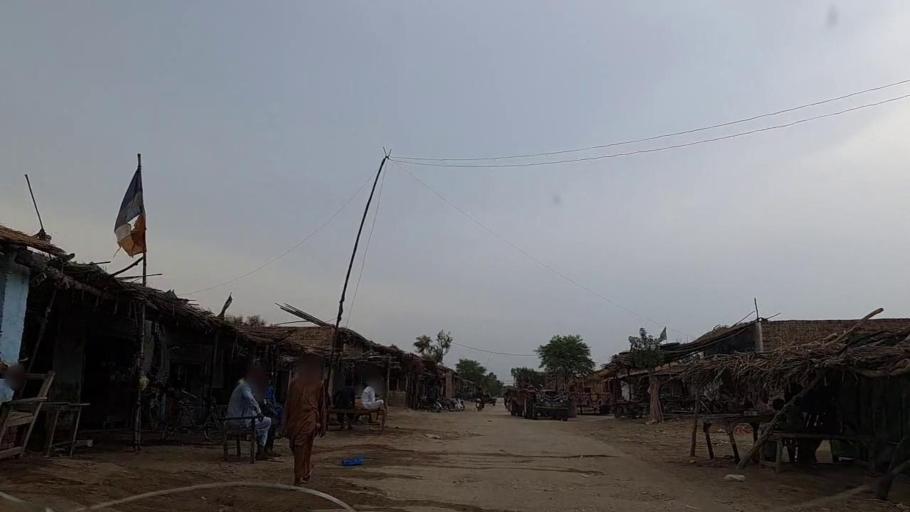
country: PK
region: Sindh
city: Mirpur Mathelo
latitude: 27.8994
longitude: 69.6569
